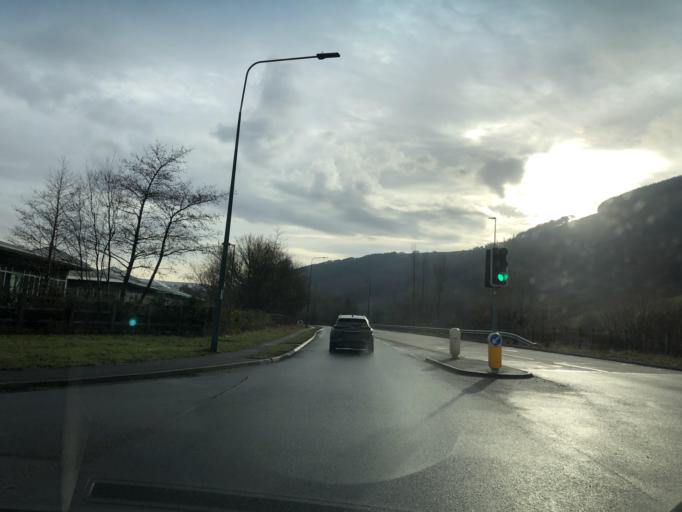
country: GB
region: Wales
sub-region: Blaenau Gwent
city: Abertillery
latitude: 51.7451
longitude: -3.1544
